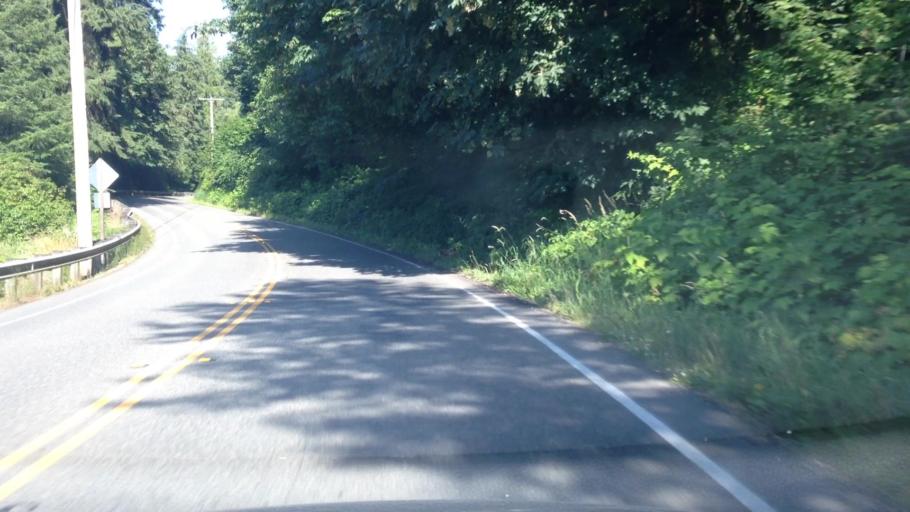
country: US
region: Washington
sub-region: King County
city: Duvall
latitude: 47.7442
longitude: -121.9378
